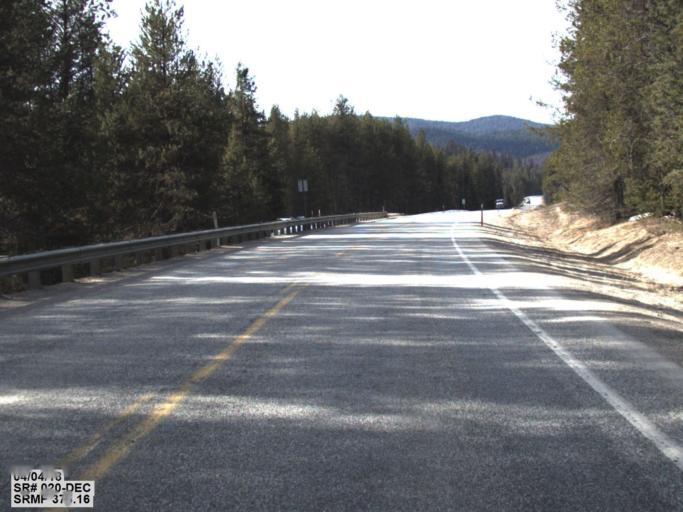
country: US
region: Washington
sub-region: Stevens County
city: Chewelah
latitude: 48.5578
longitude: -117.5581
